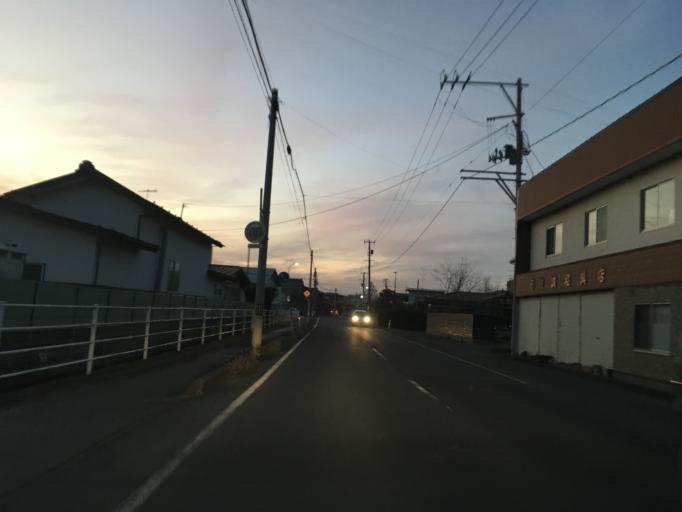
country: JP
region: Miyagi
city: Wakuya
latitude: 38.7135
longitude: 141.2220
